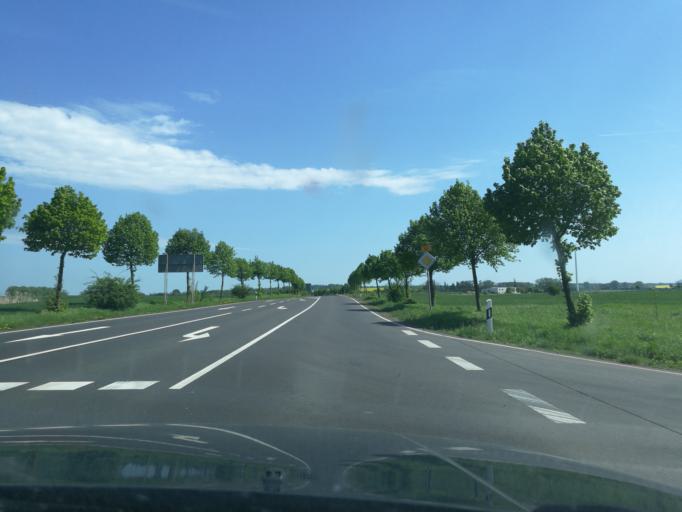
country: DE
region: Saxony-Anhalt
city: Groeningen
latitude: 51.9430
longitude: 11.2328
